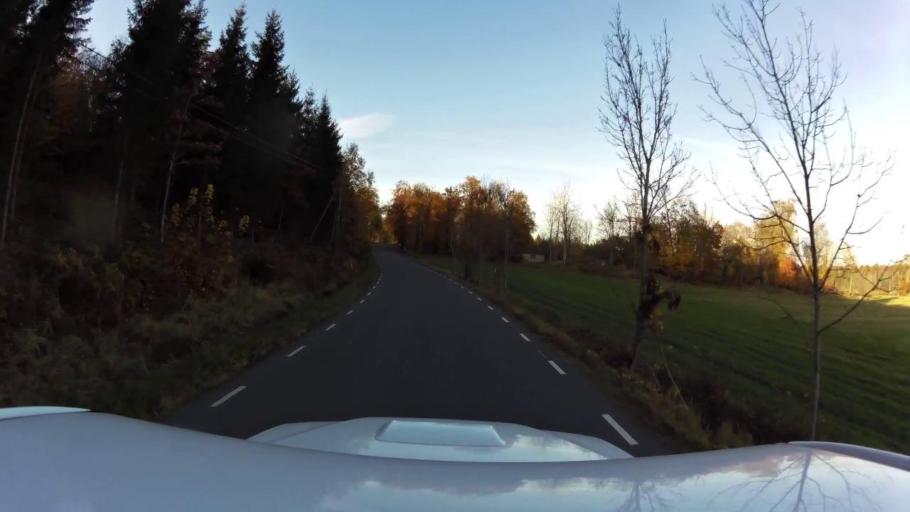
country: SE
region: OEstergoetland
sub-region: Linkopings Kommun
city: Sturefors
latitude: 58.3072
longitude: 15.6666
